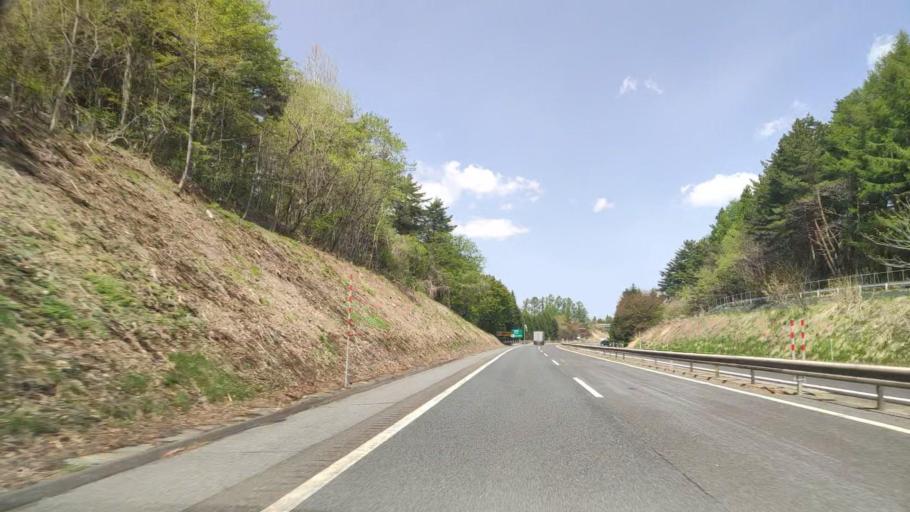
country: JP
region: Aomori
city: Hachinohe
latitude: 40.3988
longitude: 141.4462
